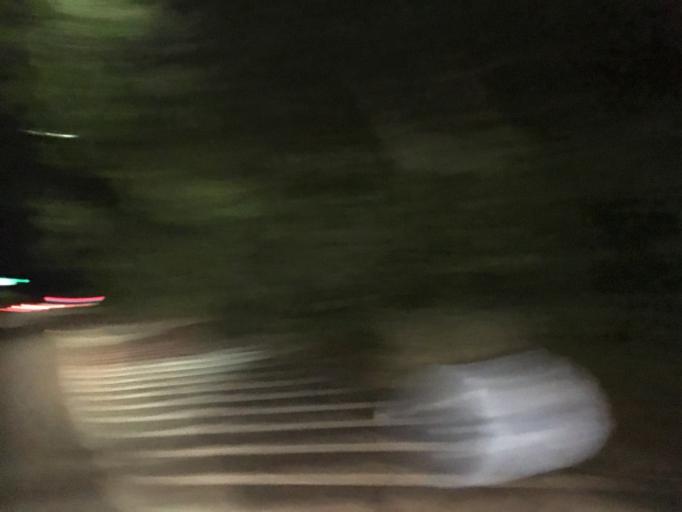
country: TW
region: Taiwan
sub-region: Hsinchu
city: Hsinchu
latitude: 24.7834
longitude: 120.9539
